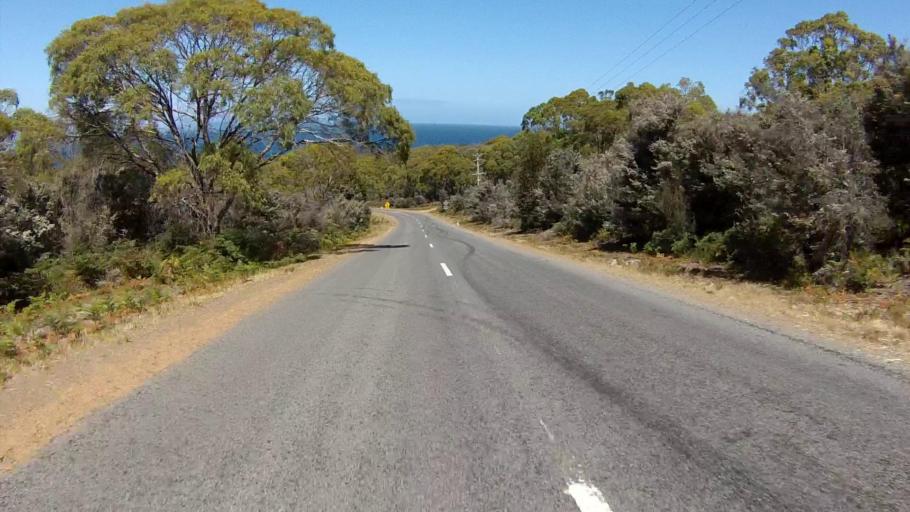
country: AU
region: Tasmania
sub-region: Clarence
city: Sandford
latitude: -43.0234
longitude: 147.4803
